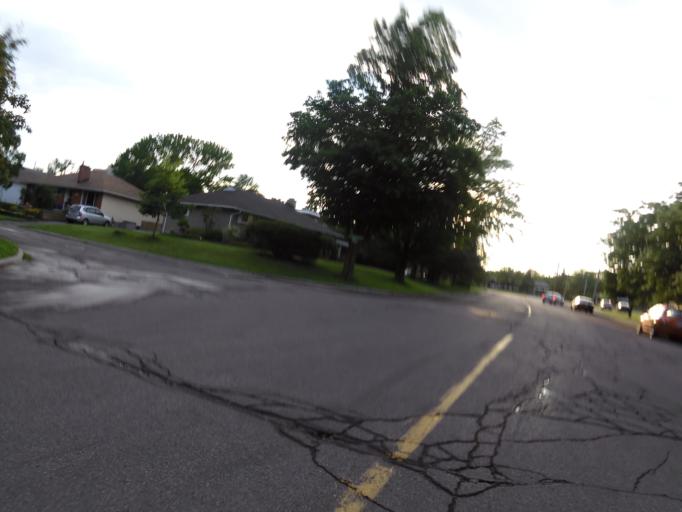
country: CA
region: Ontario
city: Ottawa
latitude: 45.3805
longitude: -75.7697
